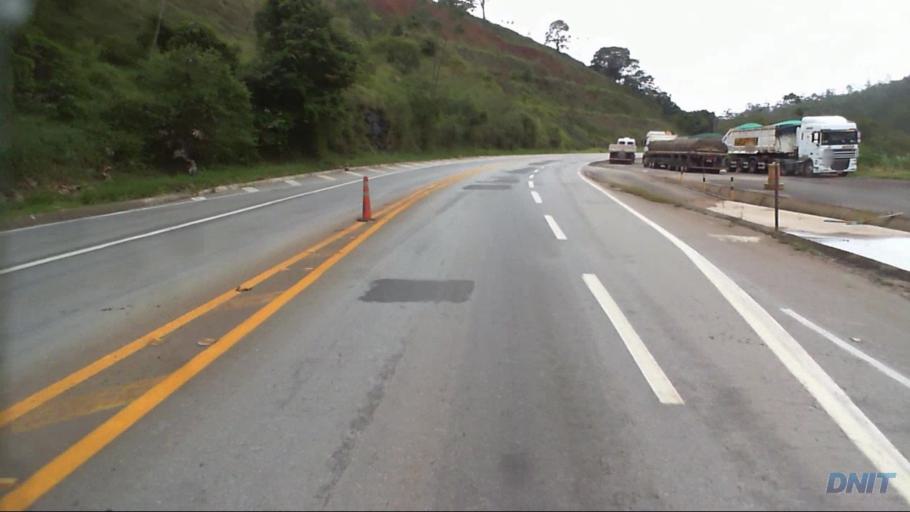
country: BR
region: Minas Gerais
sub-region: Joao Monlevade
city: Joao Monlevade
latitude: -19.8501
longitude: -43.1518
